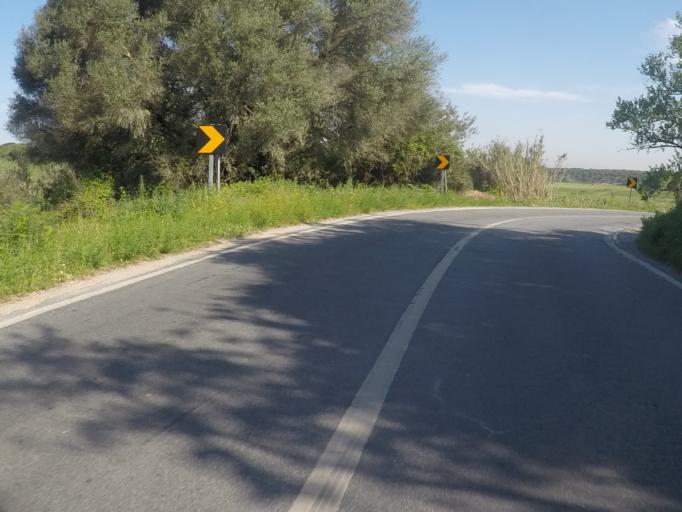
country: PT
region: Setubal
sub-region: Sesimbra
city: Sesimbra
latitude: 38.5033
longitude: -9.1488
